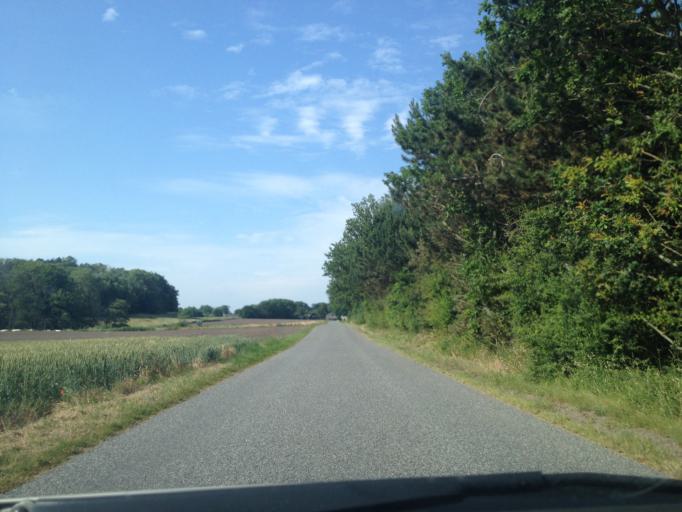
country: DK
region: Central Jutland
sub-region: Samso Kommune
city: Tranebjerg
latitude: 55.8057
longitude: 10.5563
